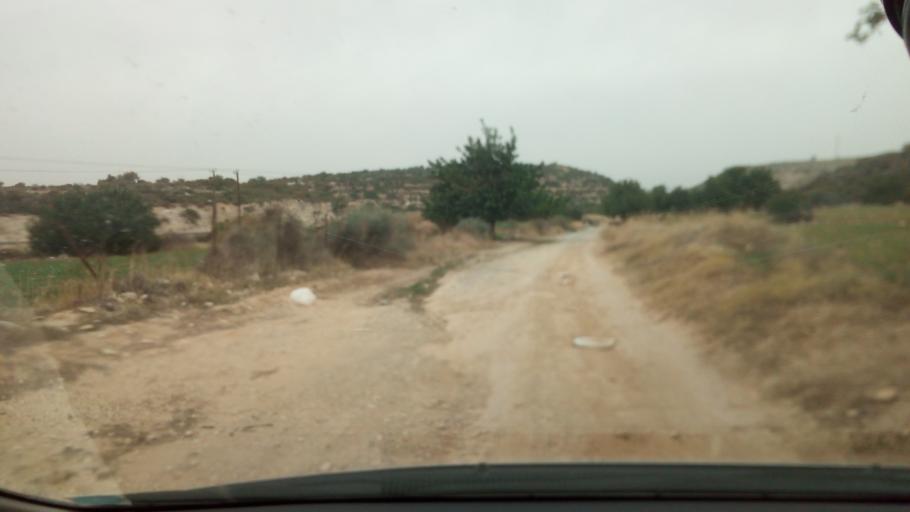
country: CY
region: Limassol
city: Ypsonas
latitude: 34.7089
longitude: 32.9563
